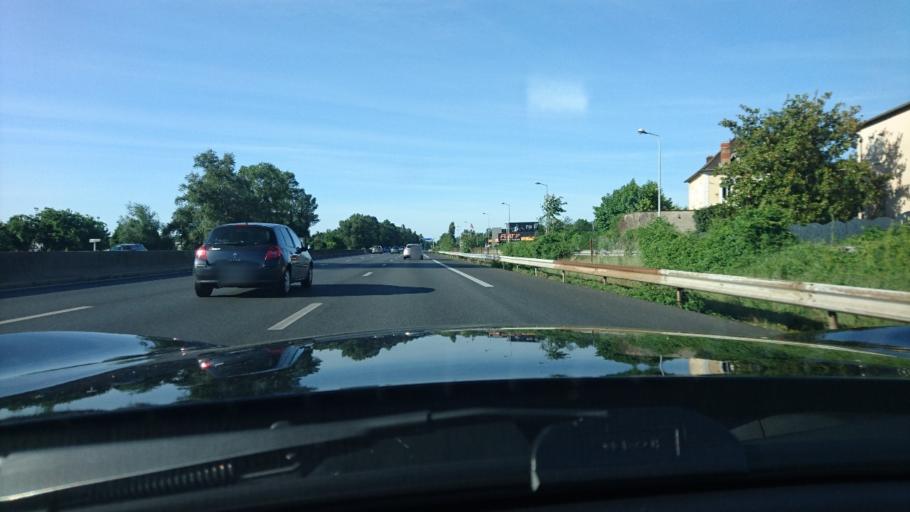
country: FR
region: Rhone-Alpes
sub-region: Departement du Rhone
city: Serezin-du-Rhone
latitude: 45.6255
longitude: 4.8156
